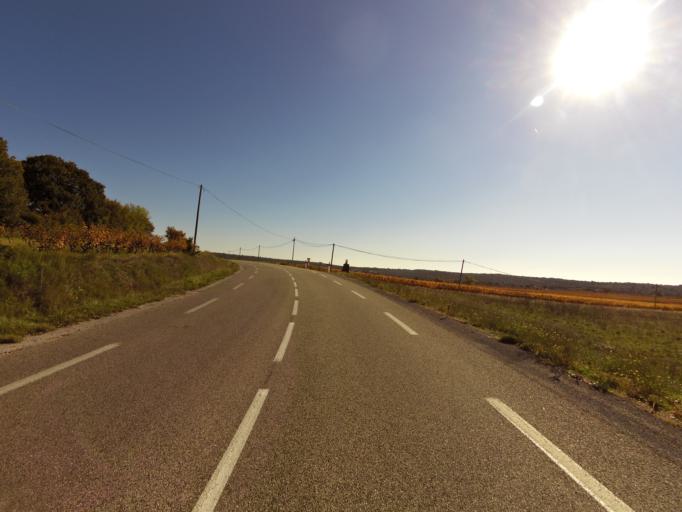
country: FR
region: Languedoc-Roussillon
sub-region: Departement du Gard
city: Saint-Julien-de-Peyrolas
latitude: 44.3980
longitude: 4.4809
